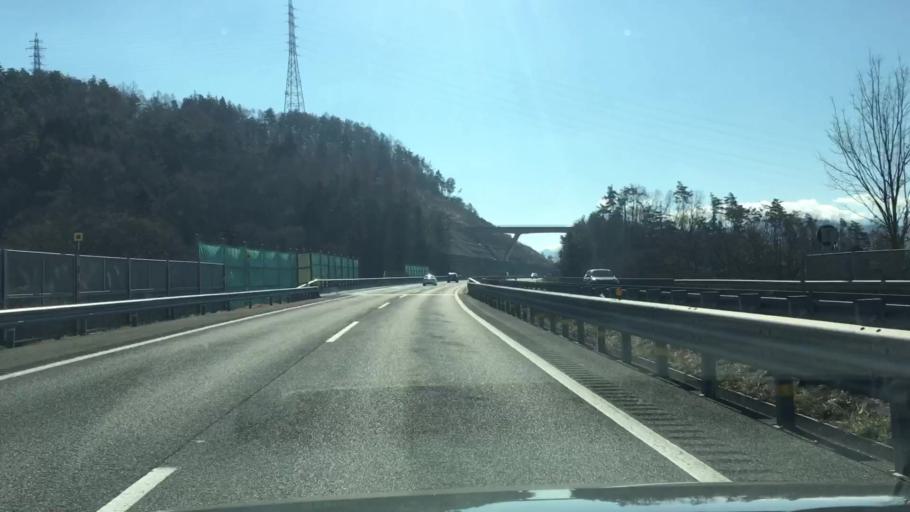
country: JP
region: Nagano
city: Ueda
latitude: 36.4699
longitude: 138.1982
